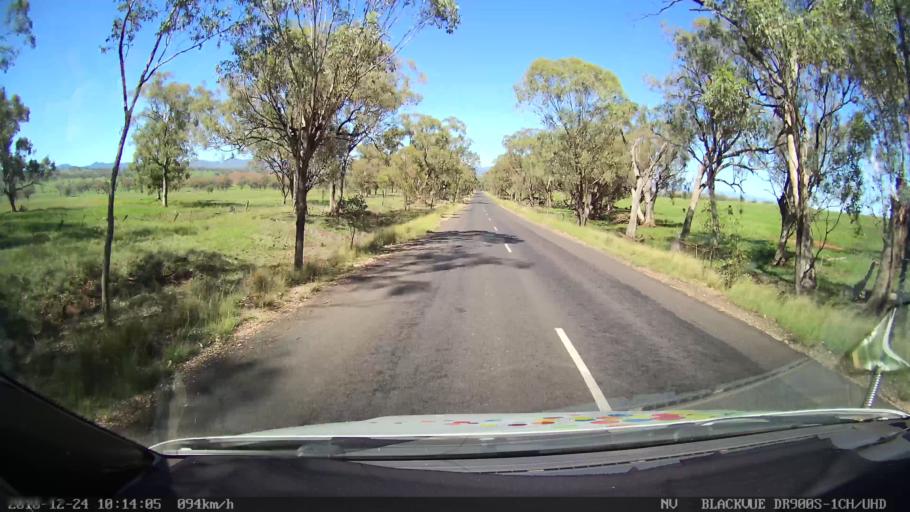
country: AU
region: New South Wales
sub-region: Liverpool Plains
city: Quirindi
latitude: -31.6950
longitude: 150.6329
